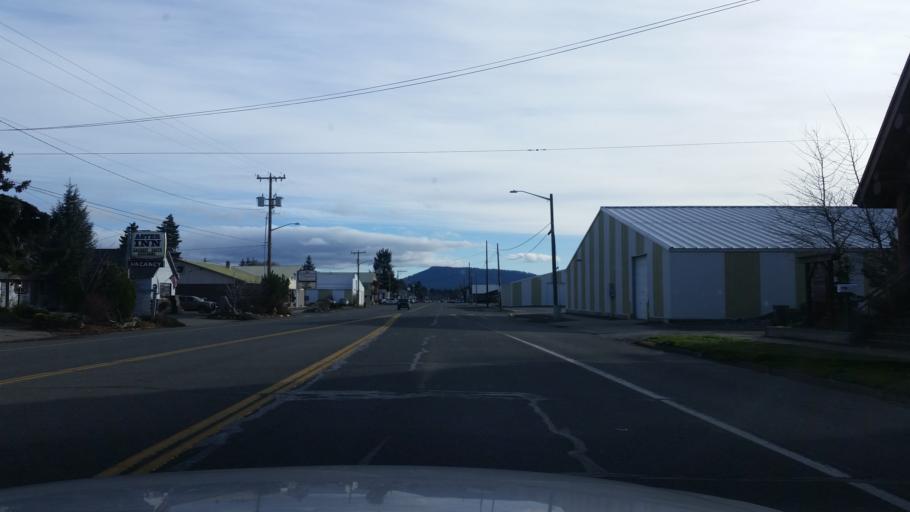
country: US
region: Washington
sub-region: Kittitas County
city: Cle Elum
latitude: 47.1938
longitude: -120.9299
